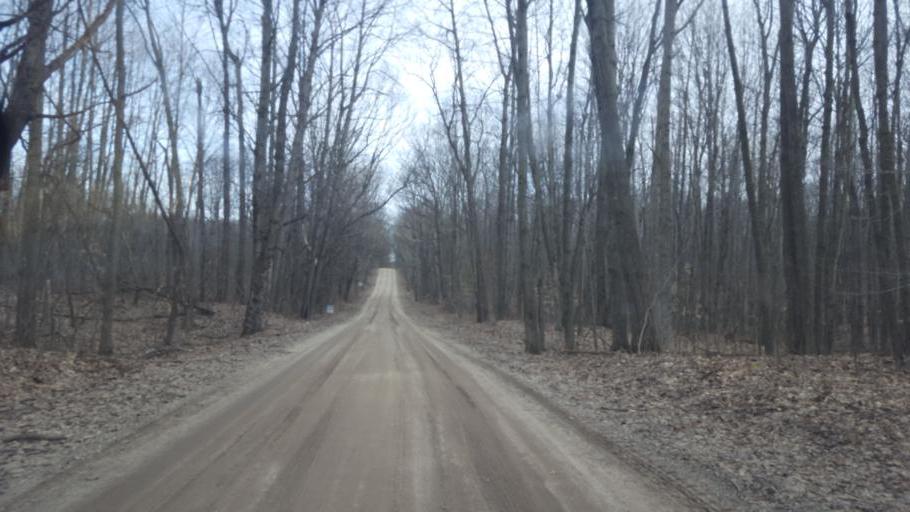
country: US
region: Michigan
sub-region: Isabella County
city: Lake Isabella
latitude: 43.6793
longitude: -85.1363
